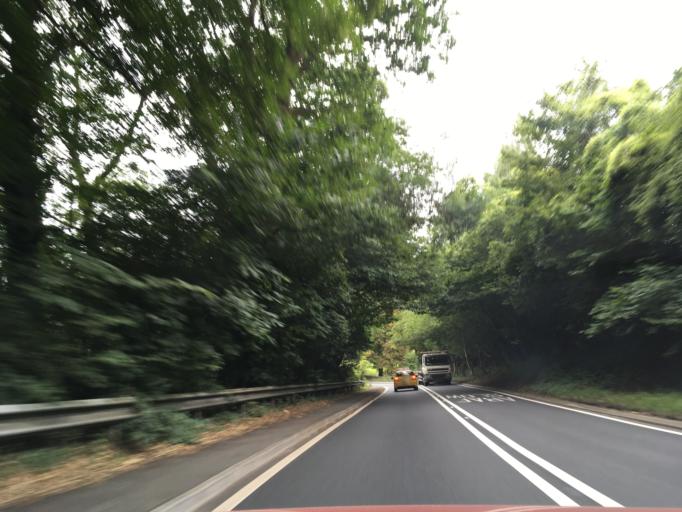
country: GB
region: Wales
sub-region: Monmouthshire
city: Gilwern
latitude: 51.8403
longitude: -3.0946
